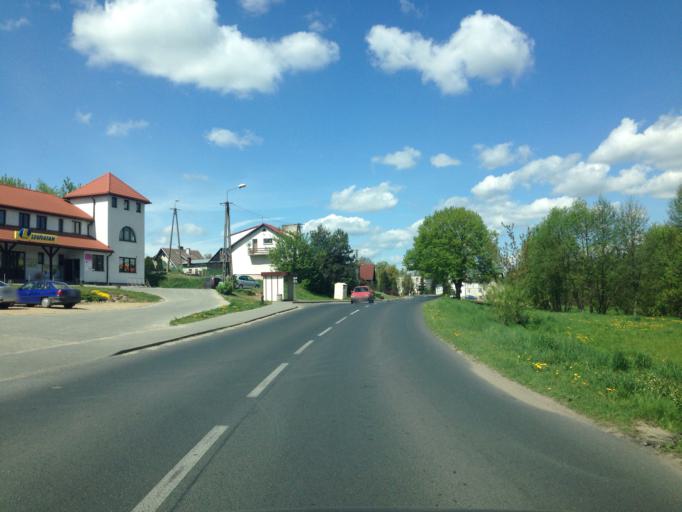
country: PL
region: Kujawsko-Pomorskie
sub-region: Powiat brodnicki
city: Bartniczka
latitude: 53.2494
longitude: 19.6062
